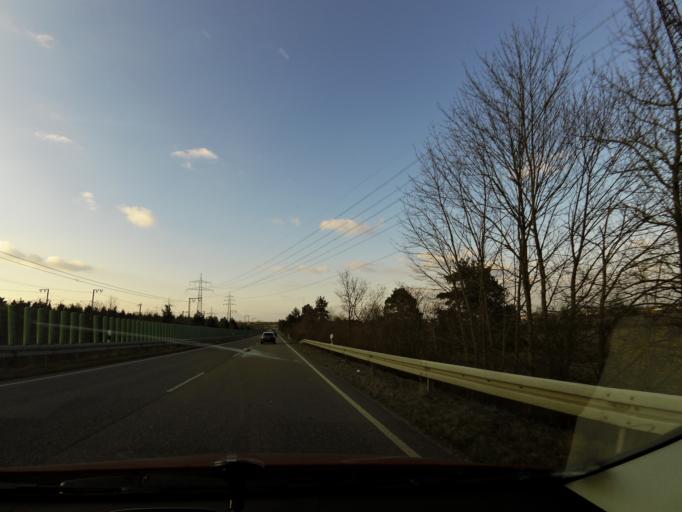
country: DE
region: Baden-Wuerttemberg
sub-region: Karlsruhe Region
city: Waghausel
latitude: 49.2164
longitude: 8.4996
